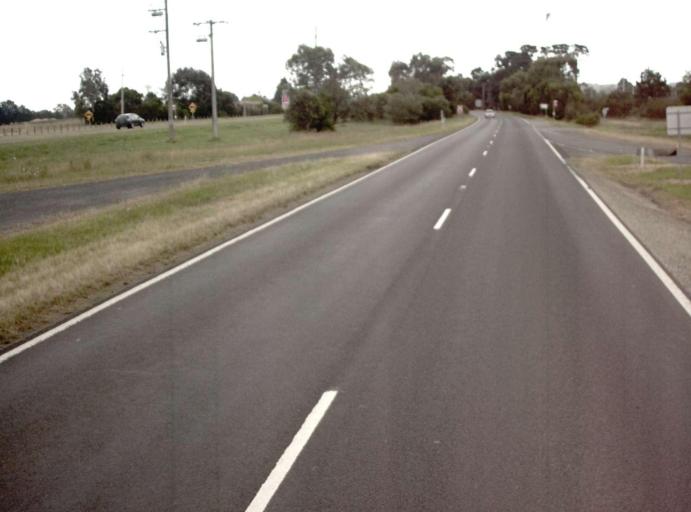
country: AU
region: Victoria
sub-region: Cardinia
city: Officer
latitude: -38.0629
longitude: 145.4205
